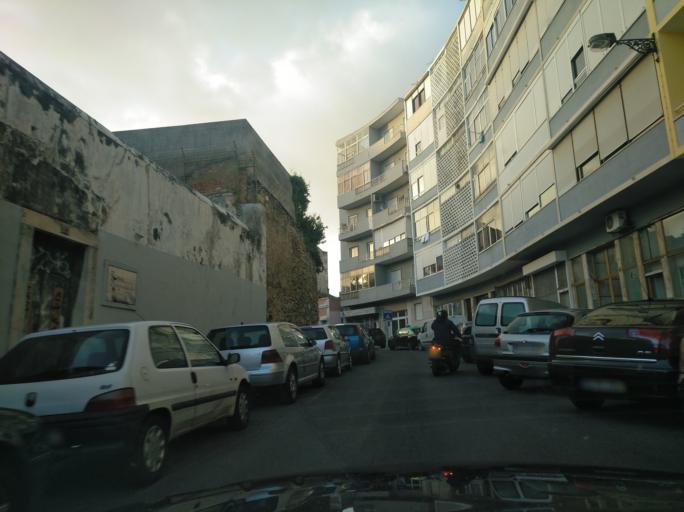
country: PT
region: Lisbon
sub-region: Lisbon
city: Lisbon
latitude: 38.7168
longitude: -9.1263
